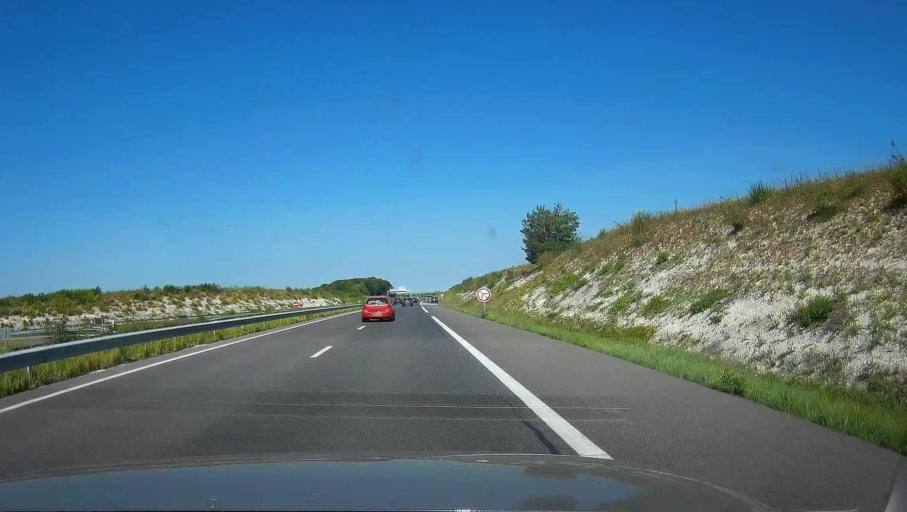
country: FR
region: Champagne-Ardenne
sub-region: Departement de la Marne
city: Fagnieres
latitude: 48.9073
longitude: 4.2844
